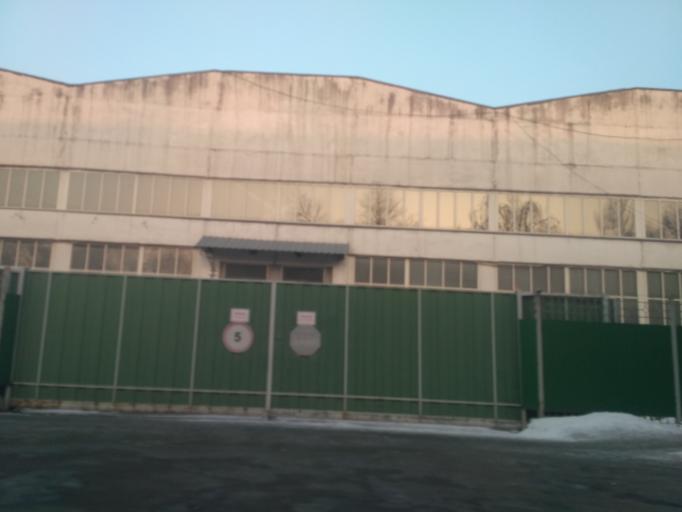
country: KZ
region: Almaty Qalasy
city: Almaty
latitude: 43.2671
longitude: 76.8631
